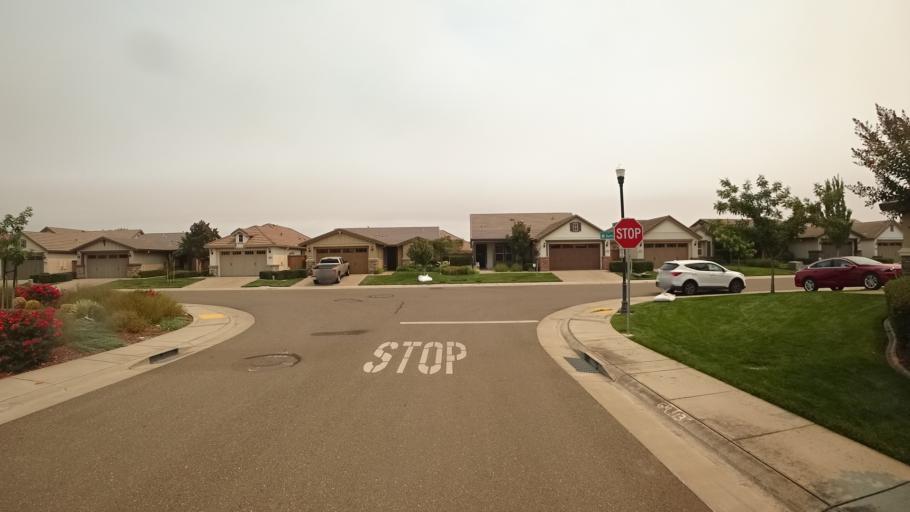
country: US
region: California
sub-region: Sacramento County
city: Laguna
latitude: 38.3965
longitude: -121.4153
